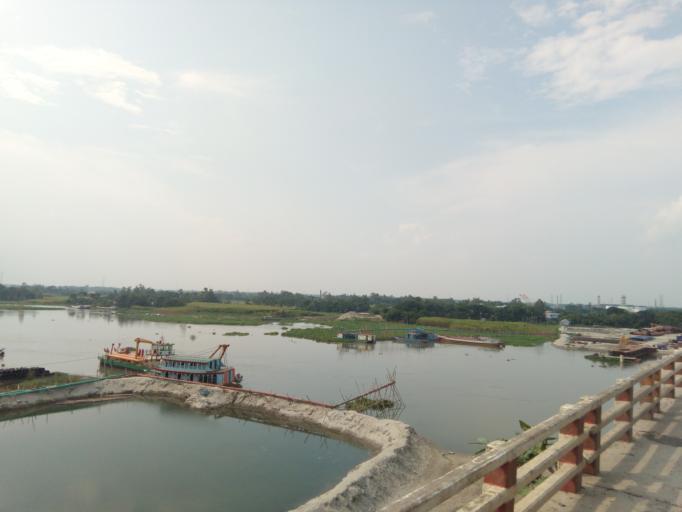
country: BD
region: Dhaka
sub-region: Dhaka
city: Dhaka
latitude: 23.6360
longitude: 90.3459
